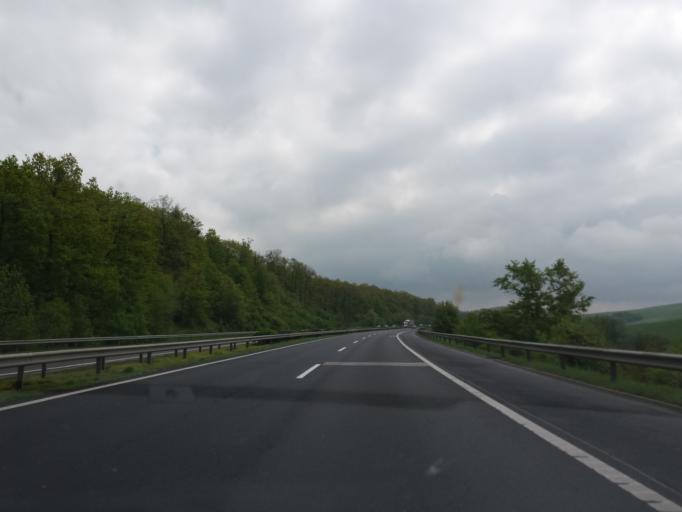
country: HU
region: Komarom-Esztergom
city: Tarjan
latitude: 47.5710
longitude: 18.4746
